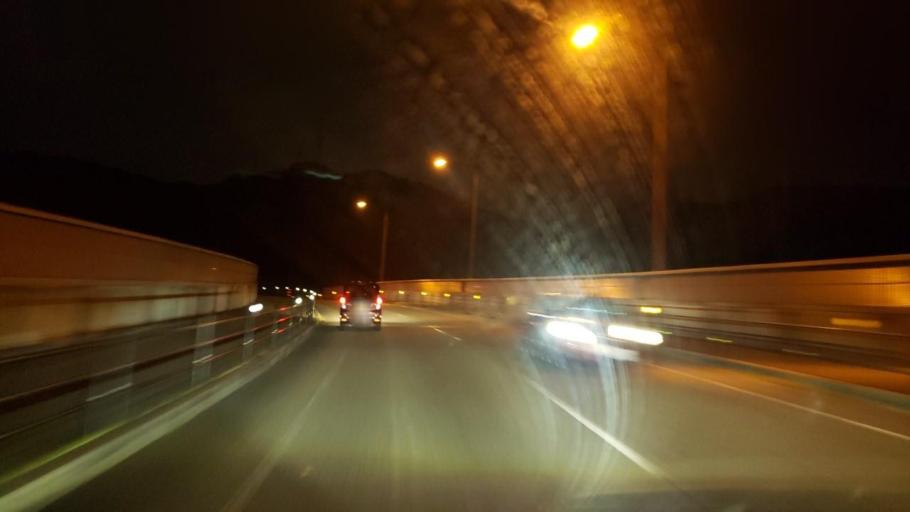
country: JP
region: Tokushima
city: Narutocho-mitsuishi
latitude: 34.1988
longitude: 134.5869
